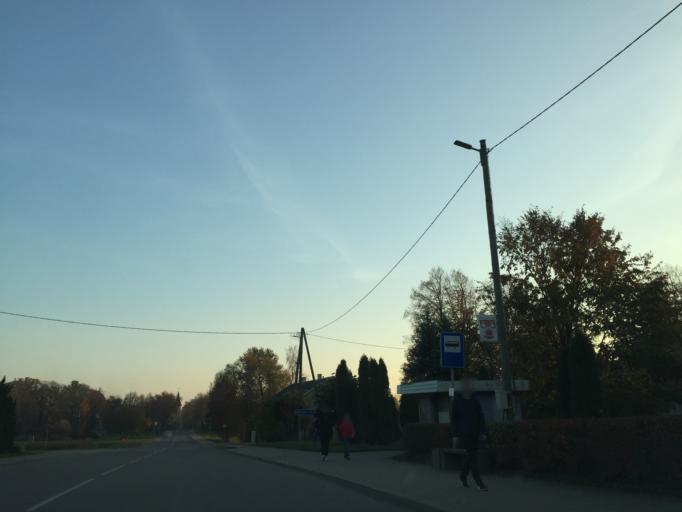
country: LV
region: Priekule
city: Priekule
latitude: 56.4466
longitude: 21.5845
